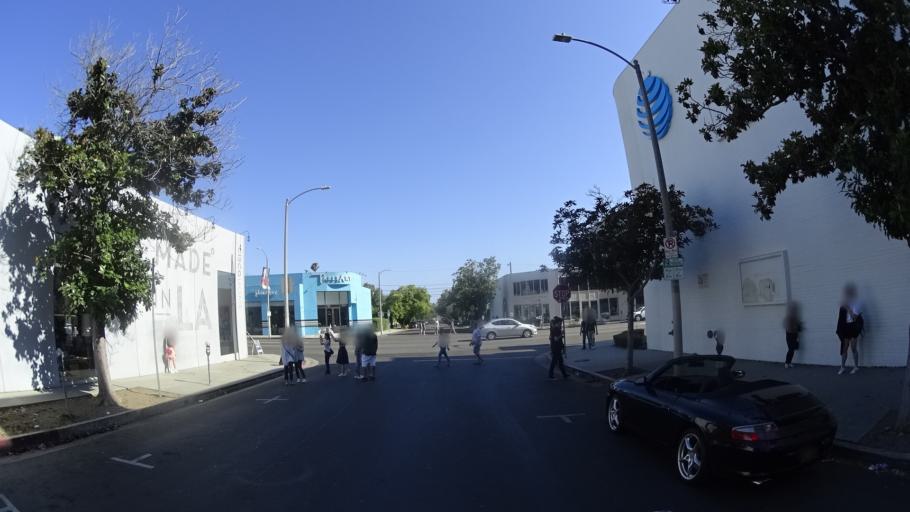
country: US
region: California
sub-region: Los Angeles County
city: West Hollywood
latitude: 34.0841
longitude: -118.3647
